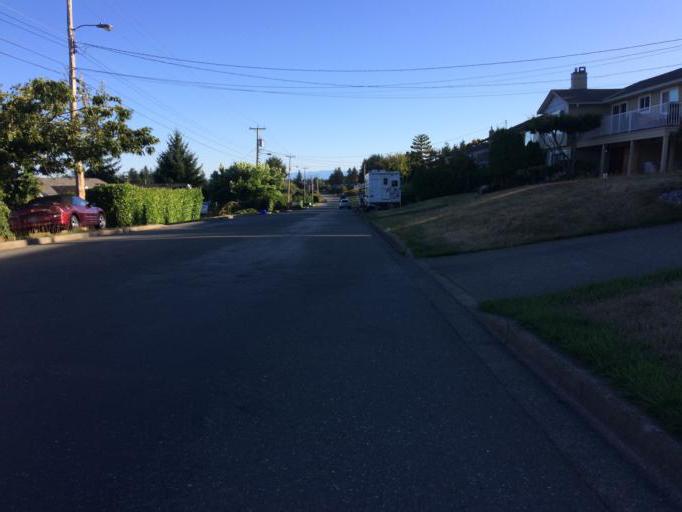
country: CA
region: British Columbia
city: Campbell River
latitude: 49.9921
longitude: -125.2319
